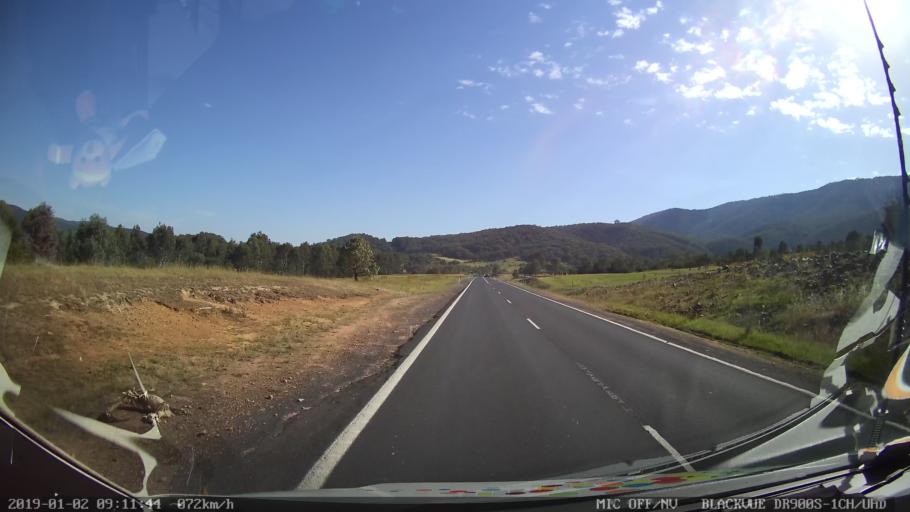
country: AU
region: New South Wales
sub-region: Tumut Shire
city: Tumut
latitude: -35.5087
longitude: 148.2703
